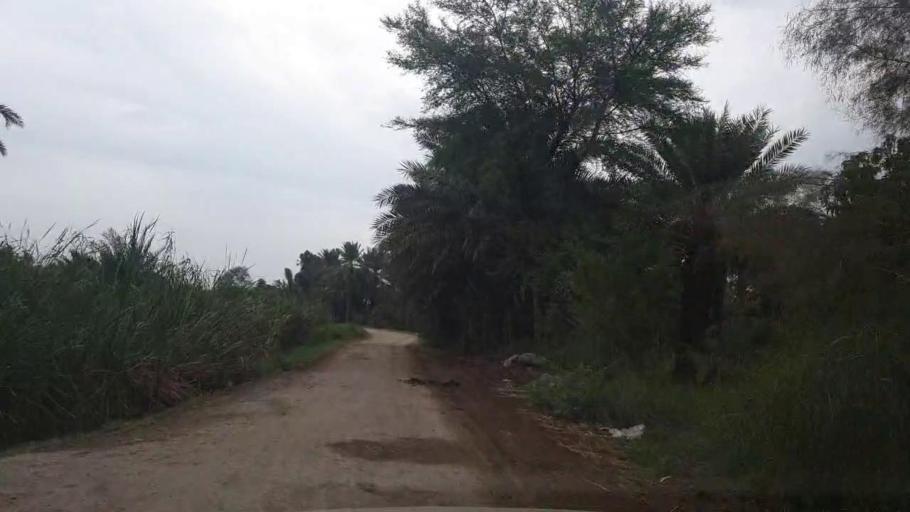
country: PK
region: Sindh
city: Khairpur
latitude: 27.5393
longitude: 68.7367
